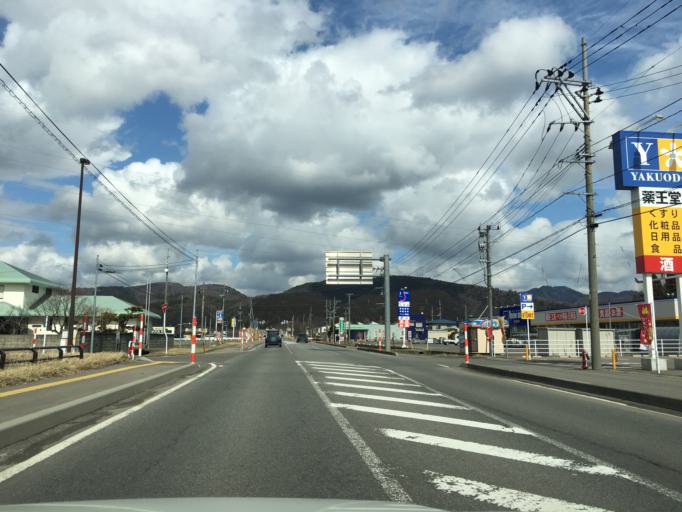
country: JP
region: Akita
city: Odate
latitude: 40.2199
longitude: 140.5865
